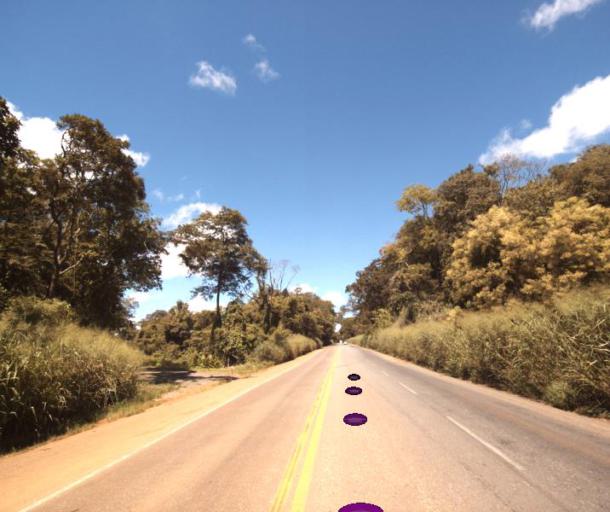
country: BR
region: Goias
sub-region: Anapolis
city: Anapolis
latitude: -16.1036
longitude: -49.0303
